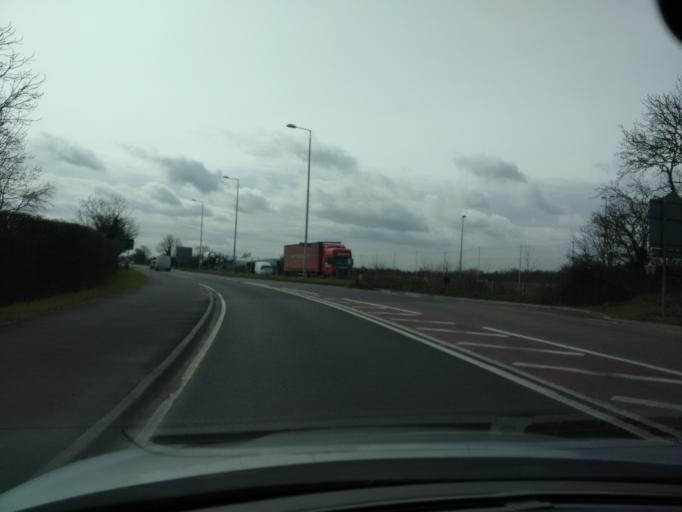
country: GB
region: England
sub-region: Worcestershire
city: Evesham
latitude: 52.0730
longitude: -1.9540
